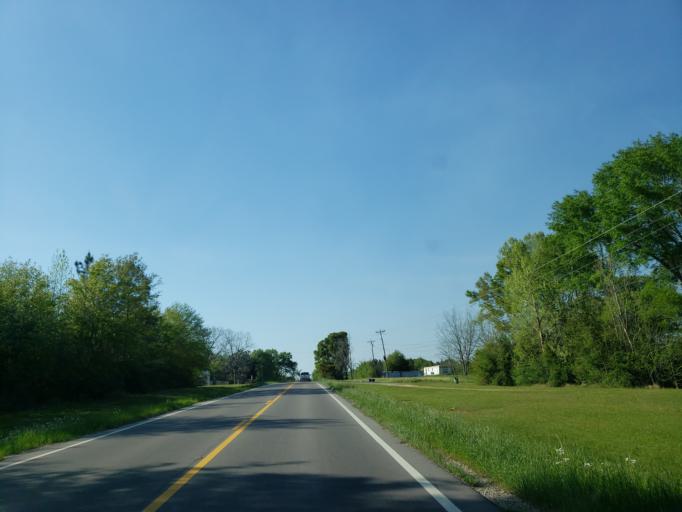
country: US
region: Mississippi
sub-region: Perry County
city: Richton
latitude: 31.4256
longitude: -88.9615
